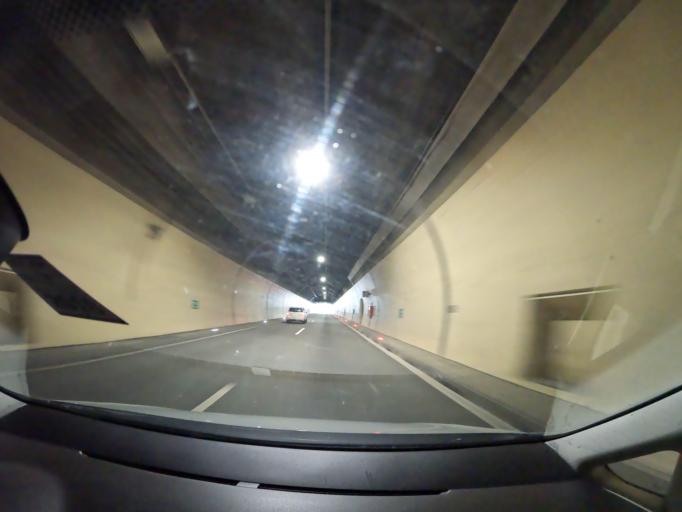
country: AT
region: Carinthia
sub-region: Politischer Bezirk Wolfsberg
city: Bad Sankt Leonhard im Lavanttal
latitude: 46.9172
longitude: 14.8255
